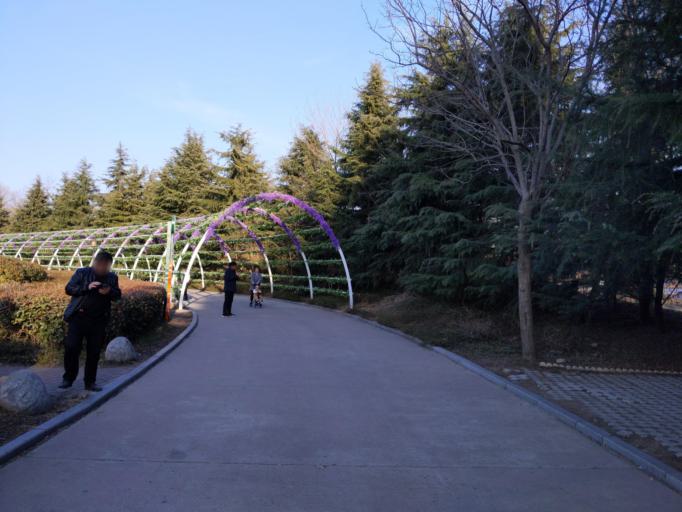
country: CN
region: Henan Sheng
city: Puyang
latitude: 35.7761
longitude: 114.9477
